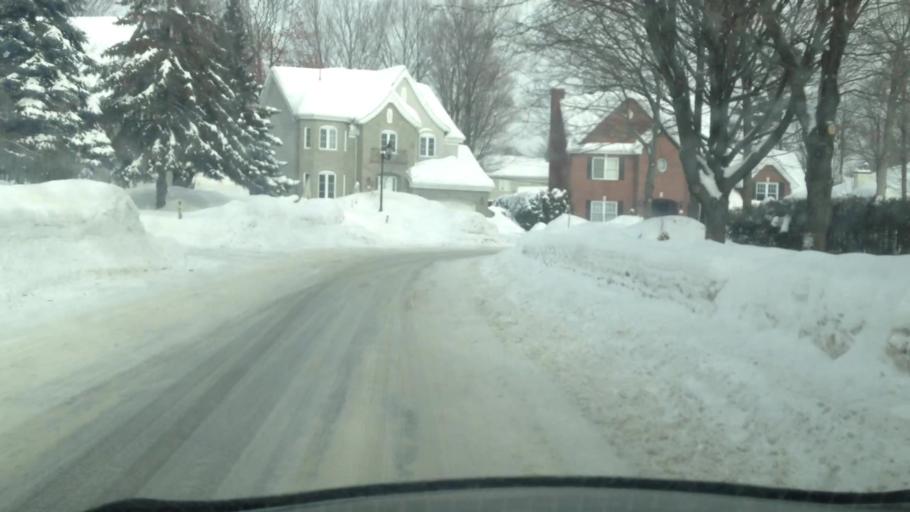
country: CA
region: Quebec
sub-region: Laurentides
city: Saint-Jerome
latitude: 45.7929
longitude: -74.0411
